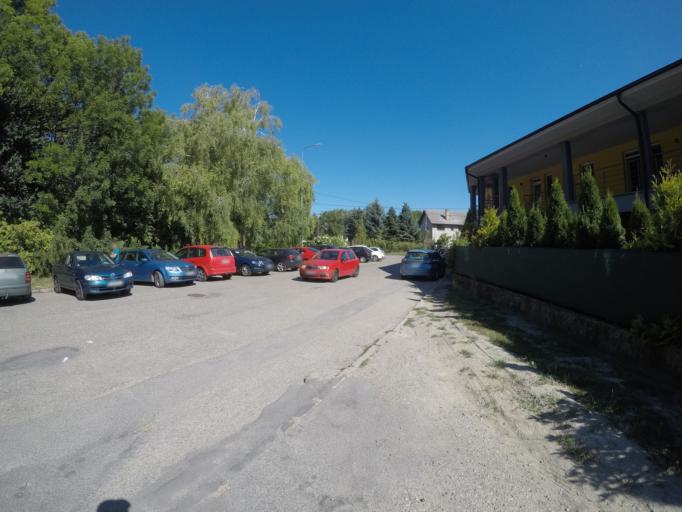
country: SK
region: Trnavsky
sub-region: Okres Dunajska Streda
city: Velky Meder
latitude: 47.8499
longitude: 17.7623
